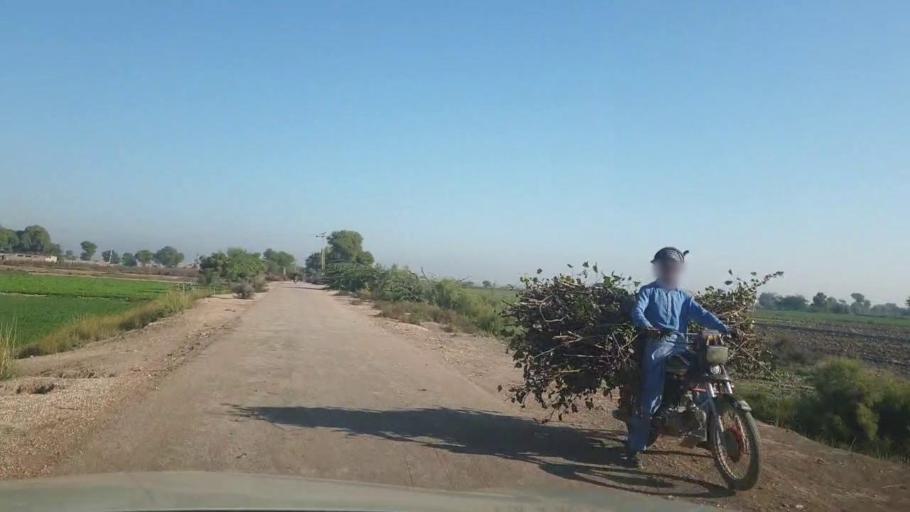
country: PK
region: Sindh
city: Bhan
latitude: 26.5442
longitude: 67.6896
